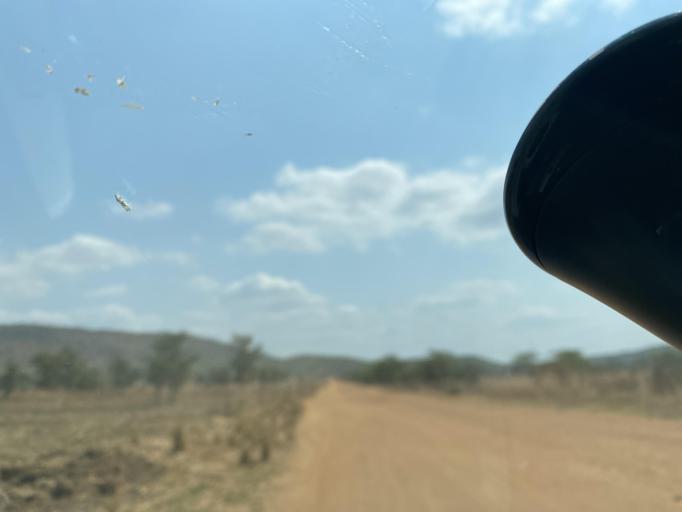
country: ZM
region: Lusaka
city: Chongwe
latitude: -15.5988
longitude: 28.7524
